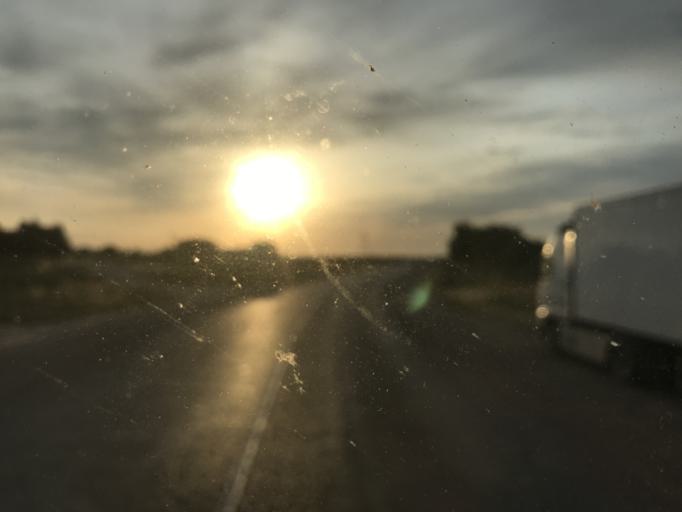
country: UZ
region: Toshkent
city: Yangiyul
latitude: 41.3349
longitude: 68.9240
